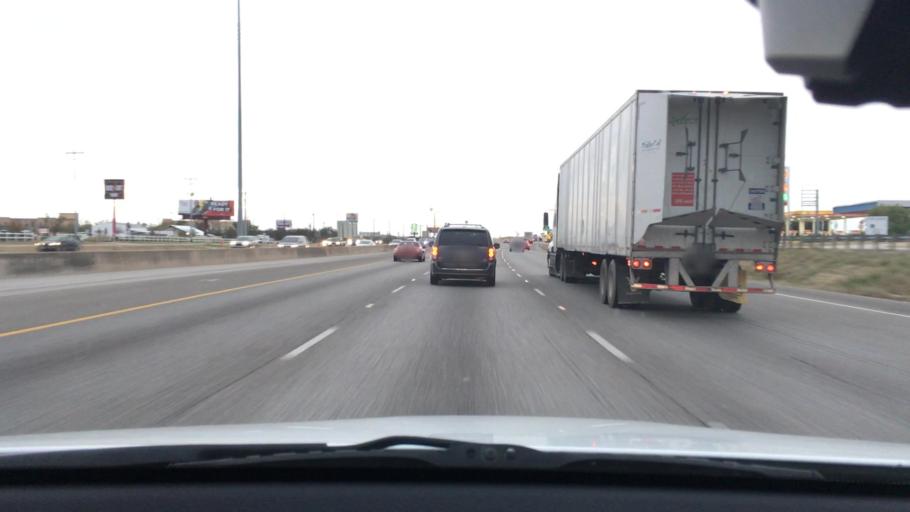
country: US
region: Texas
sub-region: Hays County
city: Buda
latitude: 30.0959
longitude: -97.8149
